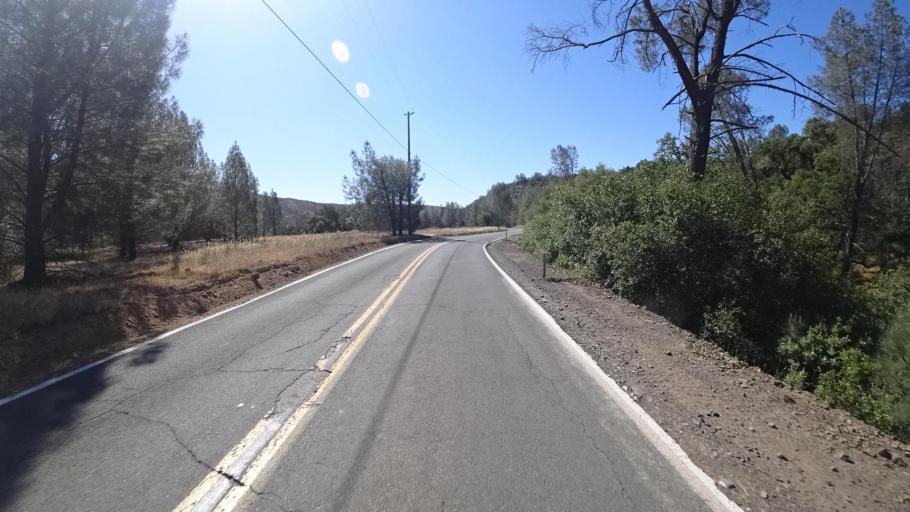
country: US
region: California
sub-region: Lake County
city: Clearlake Oaks
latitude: 39.0514
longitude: -122.5840
